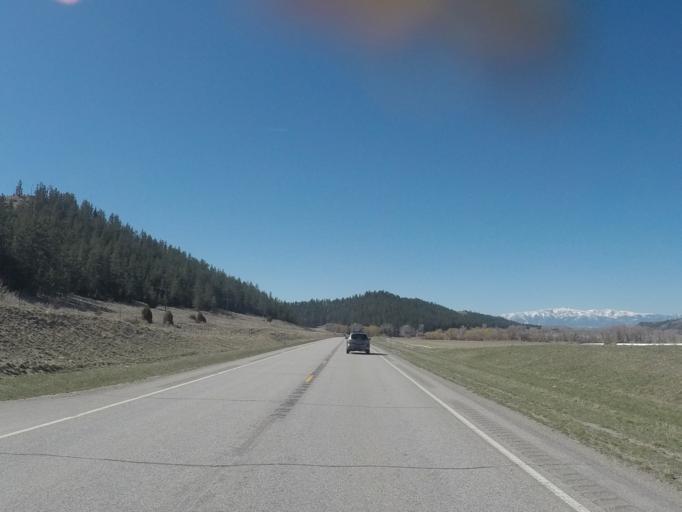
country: US
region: Montana
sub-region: Stillwater County
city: Columbus
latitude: 45.6002
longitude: -109.2914
